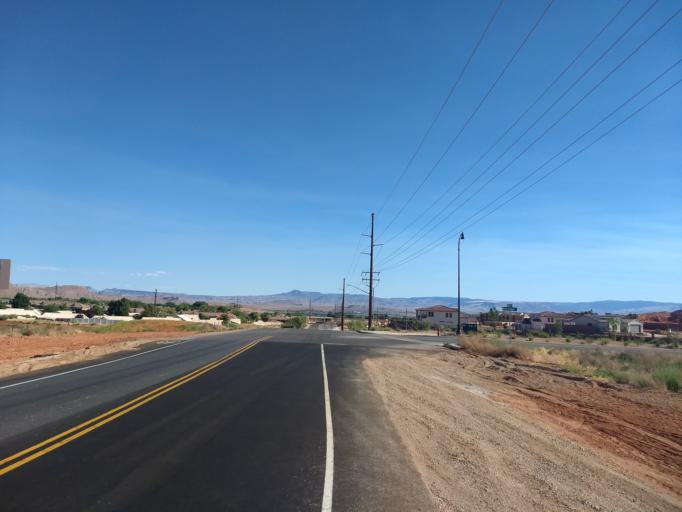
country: US
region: Utah
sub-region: Washington County
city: Washington
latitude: 37.1448
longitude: -113.5098
